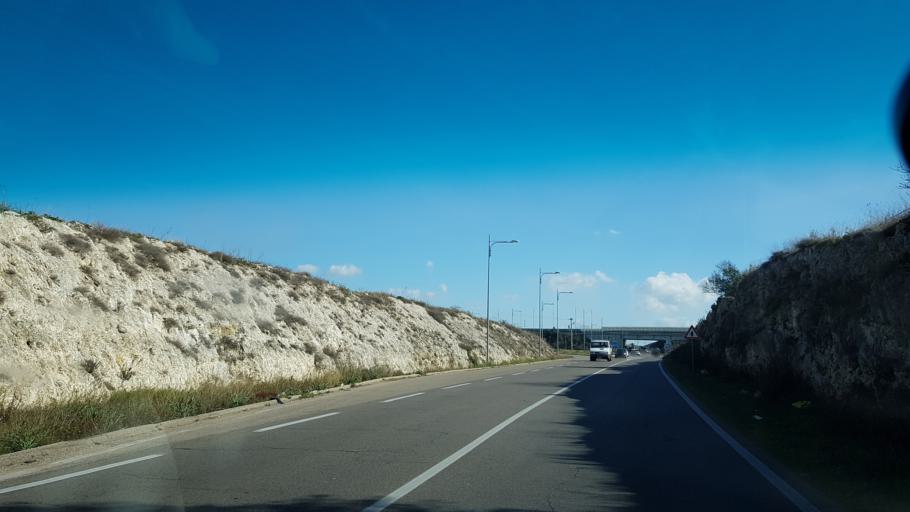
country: IT
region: Apulia
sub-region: Provincia di Lecce
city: Giorgilorio
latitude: 40.3564
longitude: 18.1311
